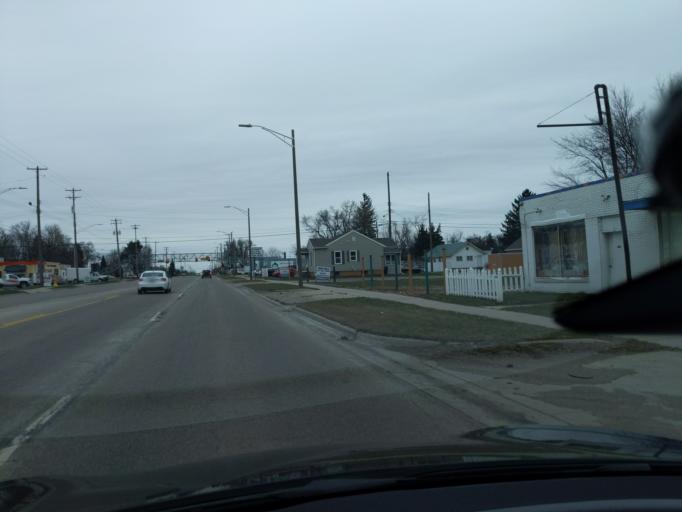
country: US
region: Michigan
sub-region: Ingham County
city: Lansing
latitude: 42.7680
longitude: -84.5426
